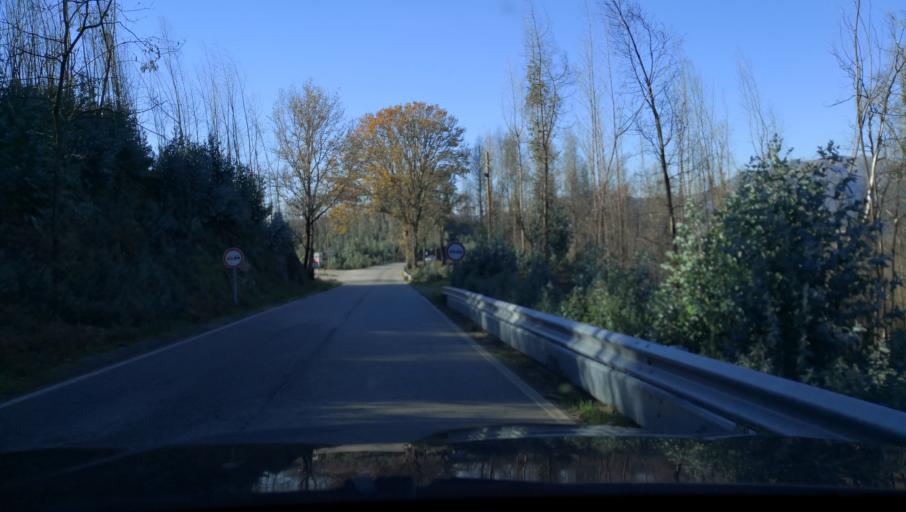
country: PT
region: Viseu
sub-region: Oliveira de Frades
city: Oliveira de Frades
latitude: 40.7306
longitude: -8.1466
